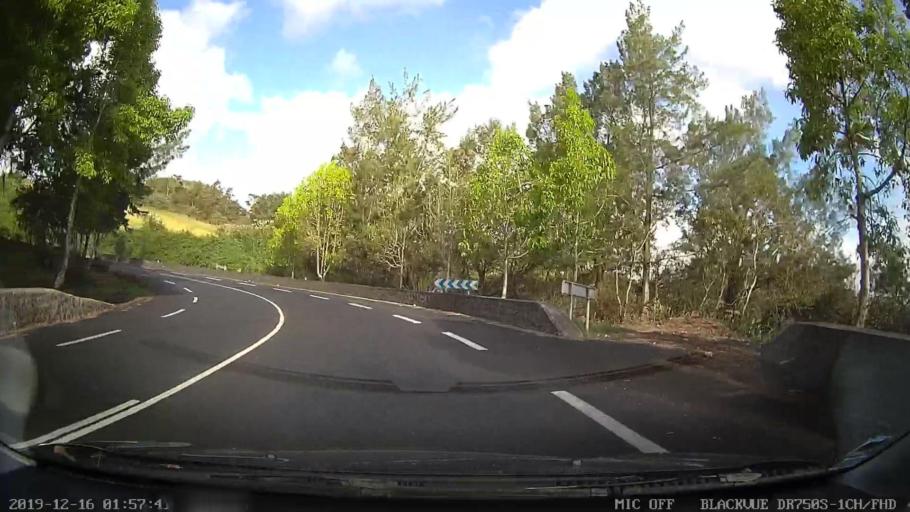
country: RE
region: Reunion
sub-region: Reunion
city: Le Tampon
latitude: -21.2337
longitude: 55.5523
